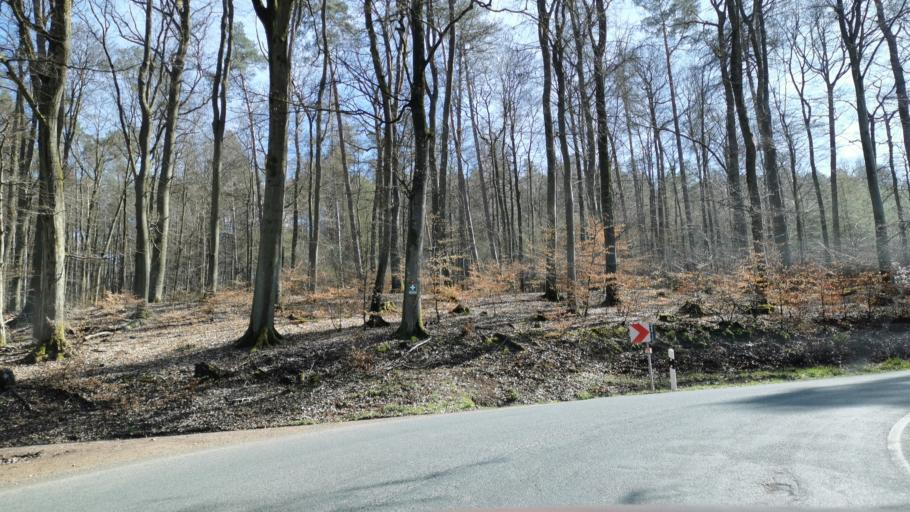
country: DE
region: Rheinland-Pfalz
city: Dreis
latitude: 49.9265
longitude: 6.8118
